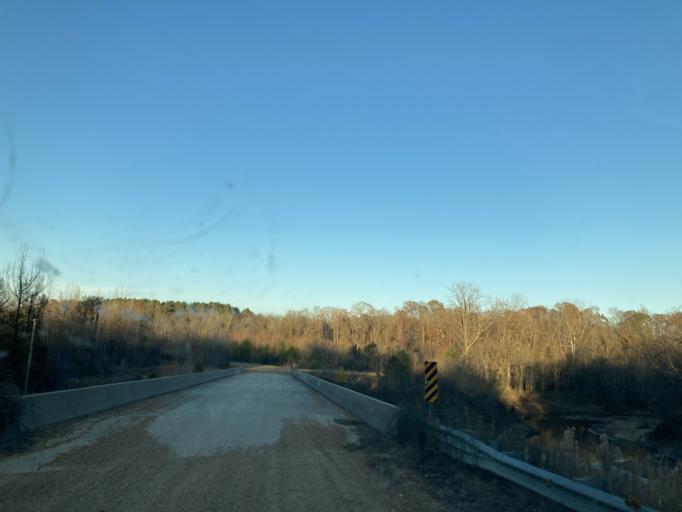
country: US
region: Mississippi
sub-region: Yazoo County
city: Yazoo City
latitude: 32.9712
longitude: -90.2666
